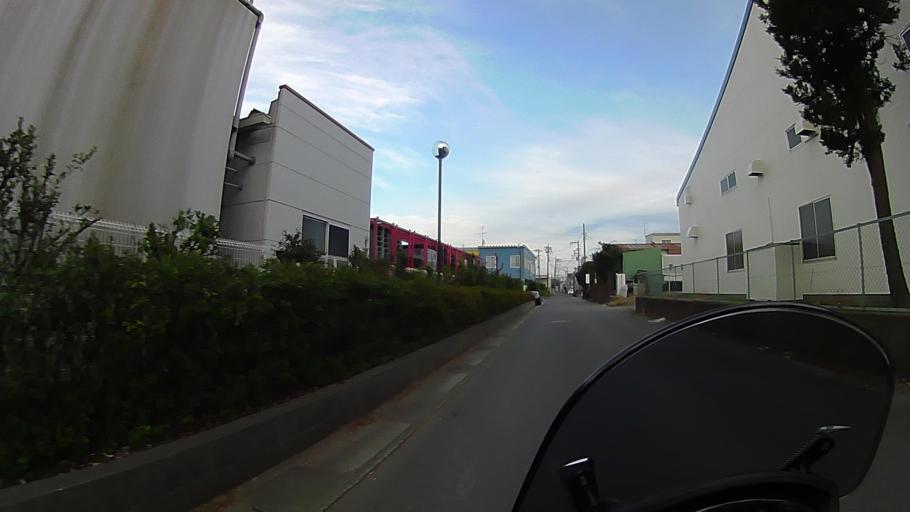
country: JP
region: Kanagawa
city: Minami-rinkan
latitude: 35.4262
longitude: 139.4238
